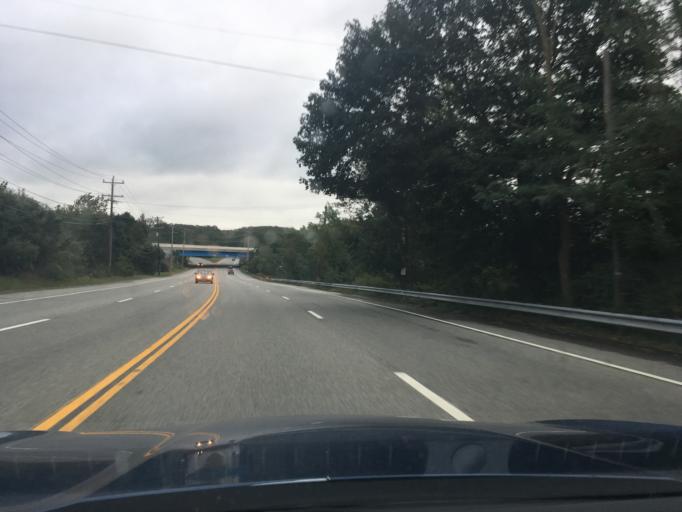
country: US
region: Rhode Island
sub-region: Kent County
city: East Greenwich
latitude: 41.6282
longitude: -71.4835
